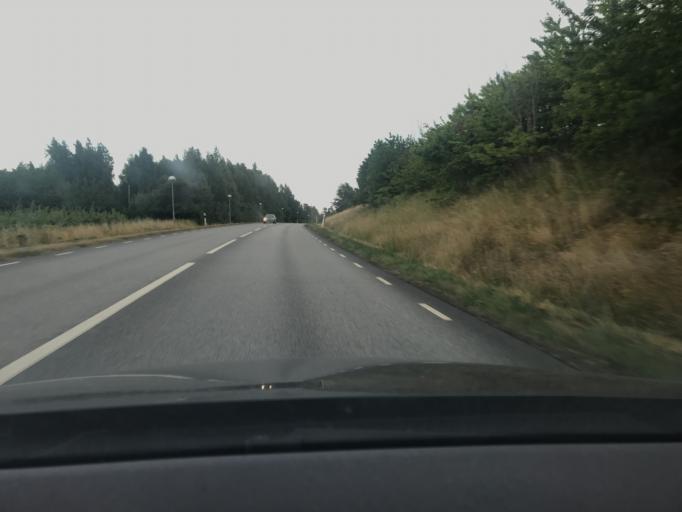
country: SE
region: Skane
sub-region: Simrishamns Kommun
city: Simrishamn
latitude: 55.5870
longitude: 14.3227
